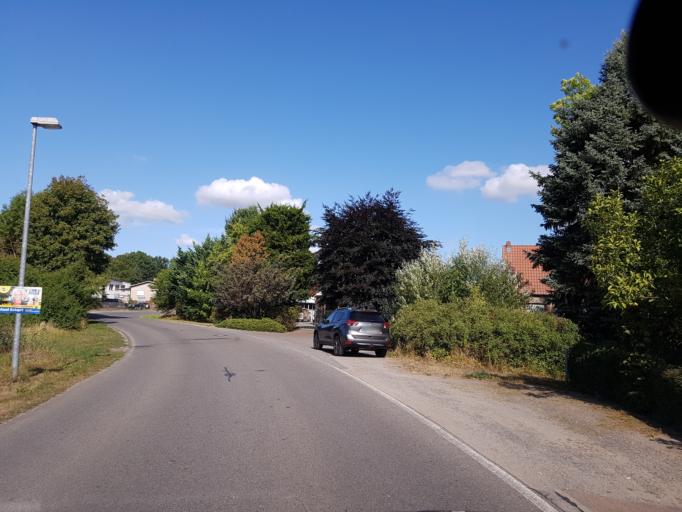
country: DE
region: Brandenburg
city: Sonnewalde
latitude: 51.6975
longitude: 13.6488
